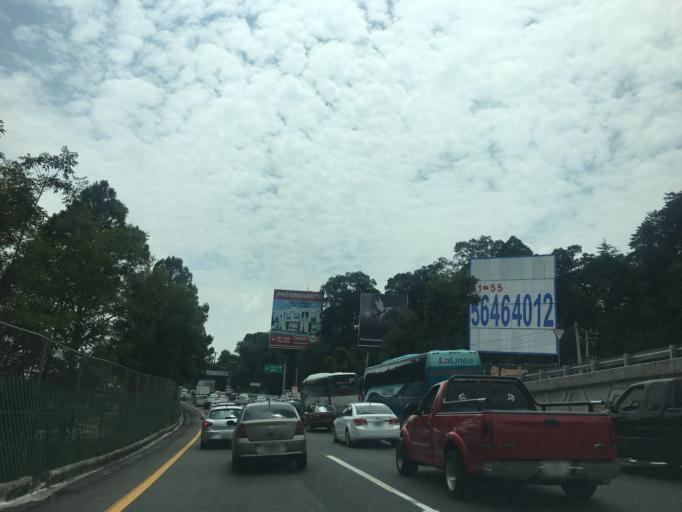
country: MX
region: Morelos
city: San Jeronimo Acazulco
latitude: 19.2924
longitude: -99.4300
